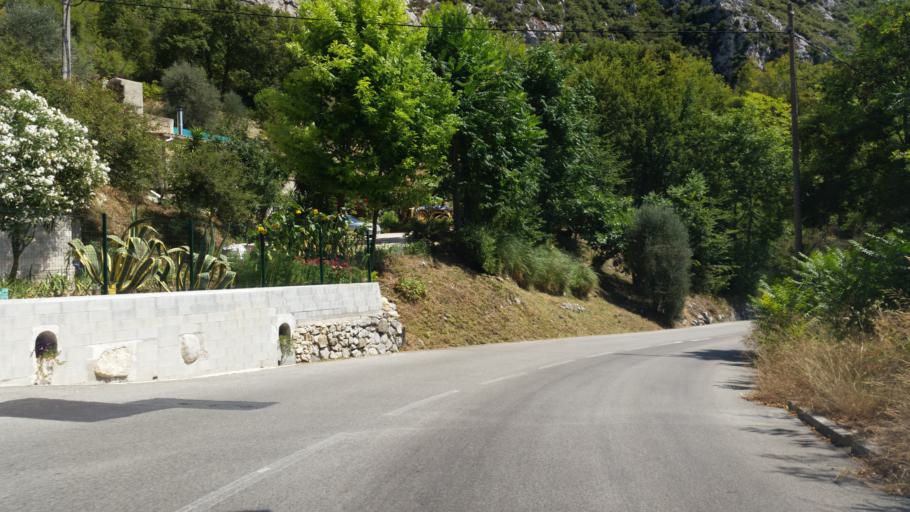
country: FR
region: Provence-Alpes-Cote d'Azur
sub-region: Departement des Alpes-Maritimes
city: Sainte-Agnes
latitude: 43.8304
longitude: 7.4778
